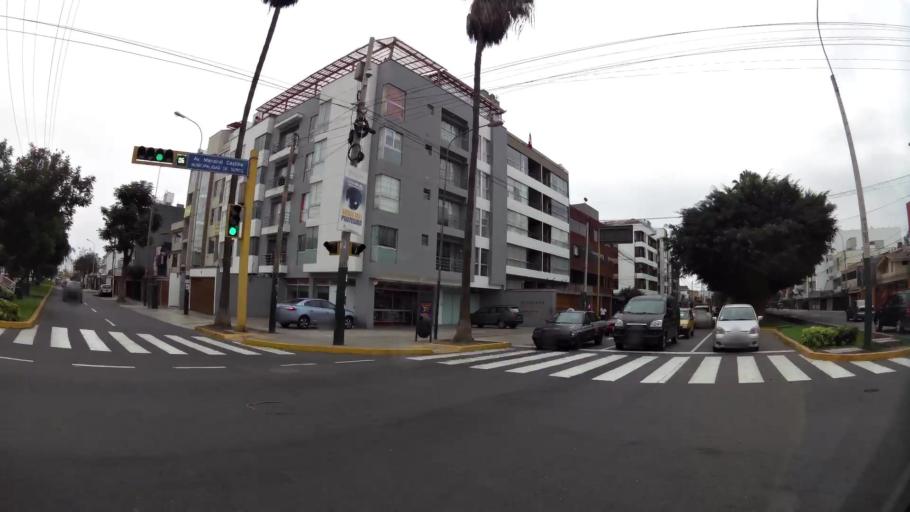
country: PE
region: Lima
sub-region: Lima
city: Surco
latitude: -12.1346
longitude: -77.0098
